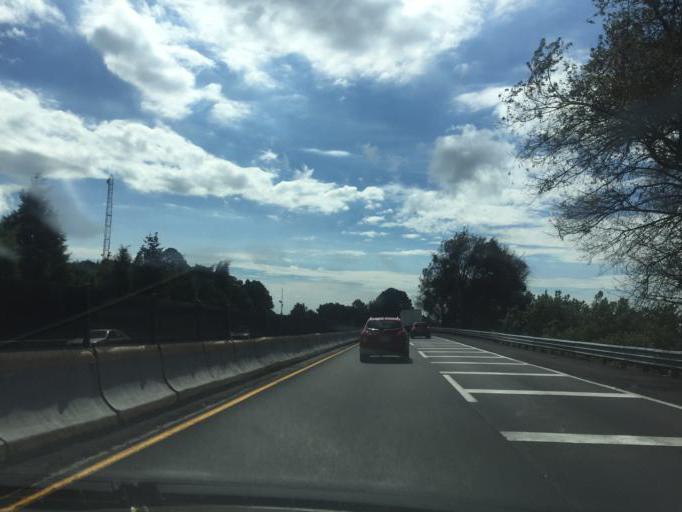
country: MX
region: Morelos
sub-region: Cuernavaca
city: Villa Santiago
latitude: 19.0261
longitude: -99.1973
